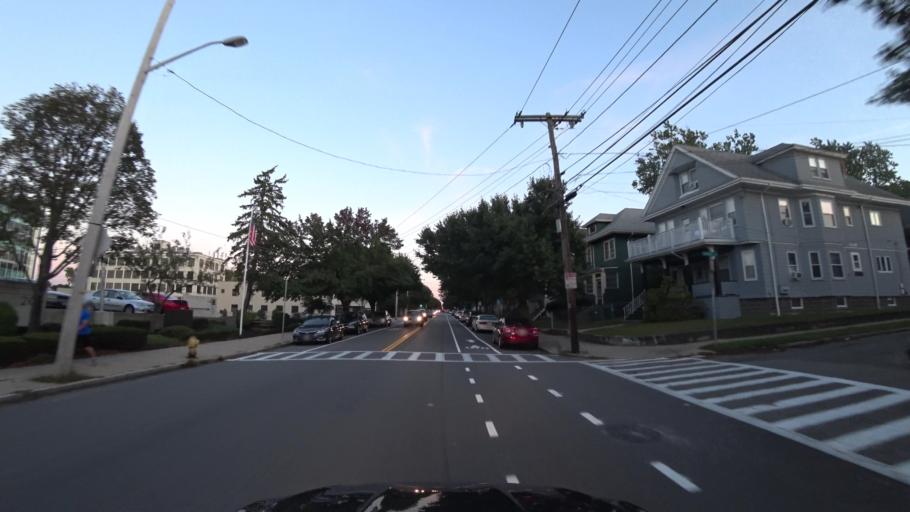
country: US
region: Massachusetts
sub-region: Middlesex County
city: Medford
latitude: 42.4152
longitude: -71.1272
